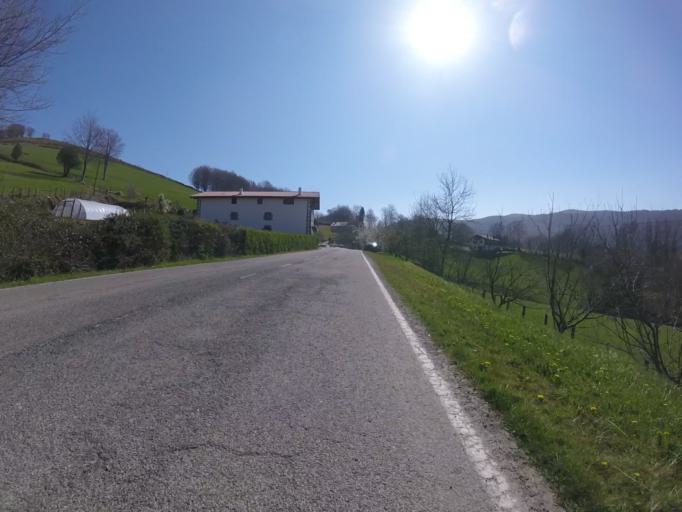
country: ES
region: Navarre
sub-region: Provincia de Navarra
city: Leitza
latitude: 43.0881
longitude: -1.8871
